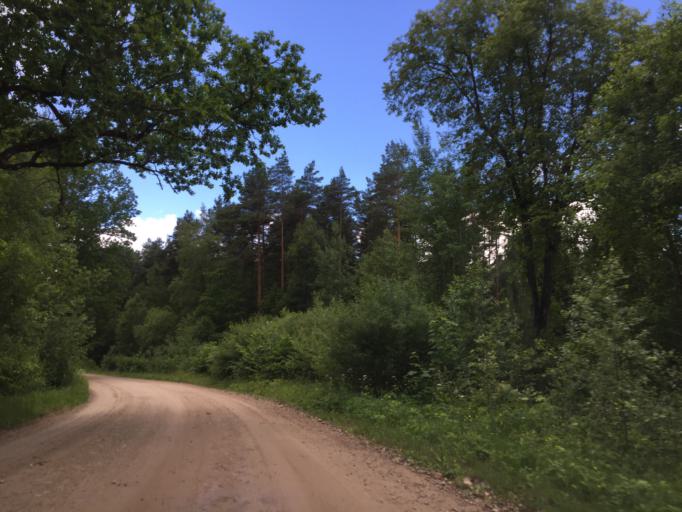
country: LV
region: Lecava
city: Iecava
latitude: 56.6209
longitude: 24.1778
